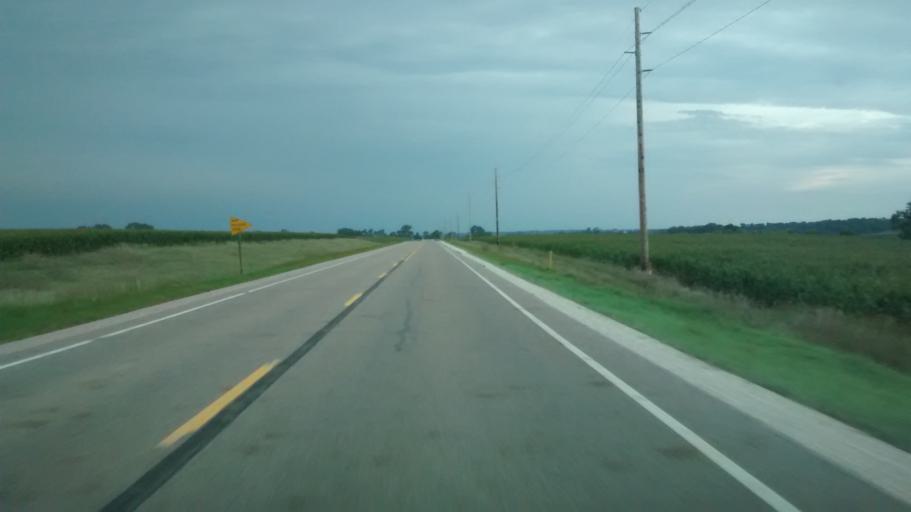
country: US
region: Iowa
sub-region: Plymouth County
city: Kingsley
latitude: 42.5696
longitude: -95.9997
